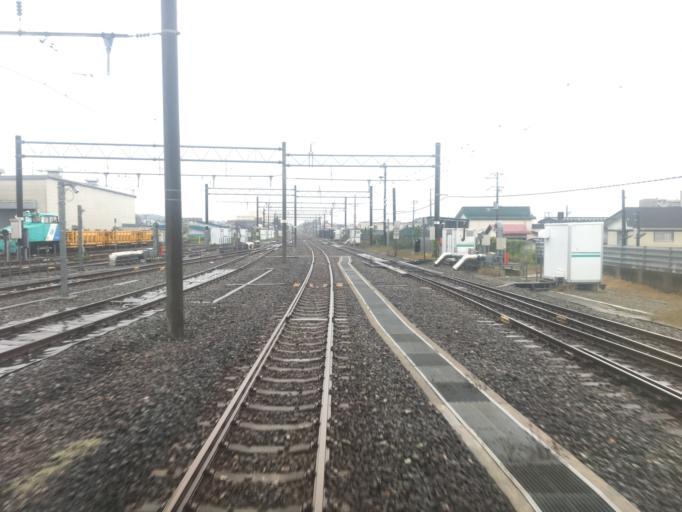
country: JP
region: Yamagata
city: Shinjo
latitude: 38.7601
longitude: 140.3065
